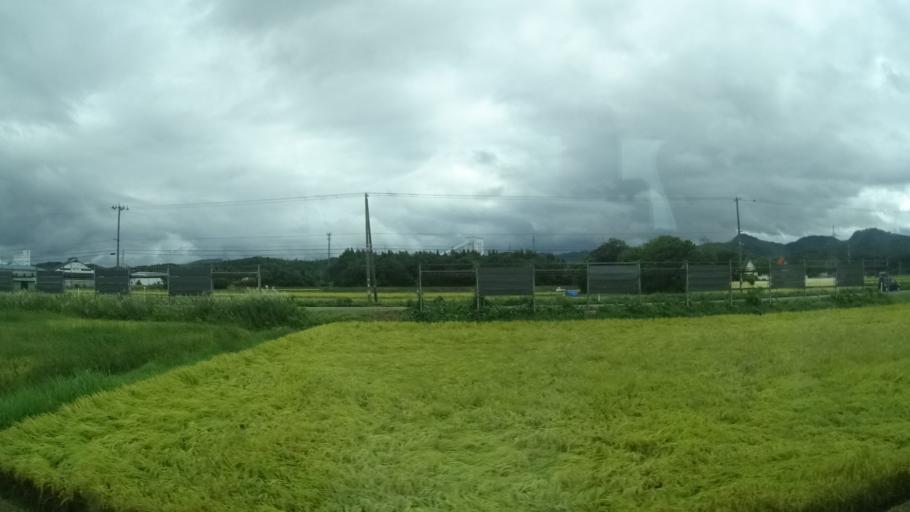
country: JP
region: Niigata
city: Murakami
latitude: 38.1559
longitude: 139.4592
